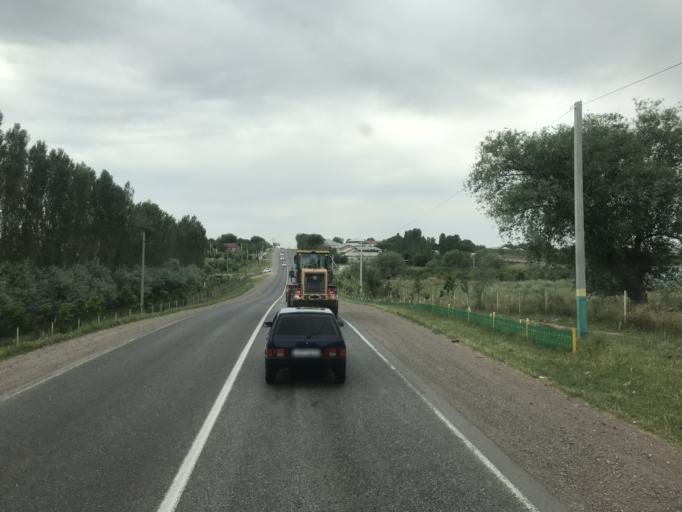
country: UZ
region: Toshkent
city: Salor
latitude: 41.4947
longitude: 69.3277
